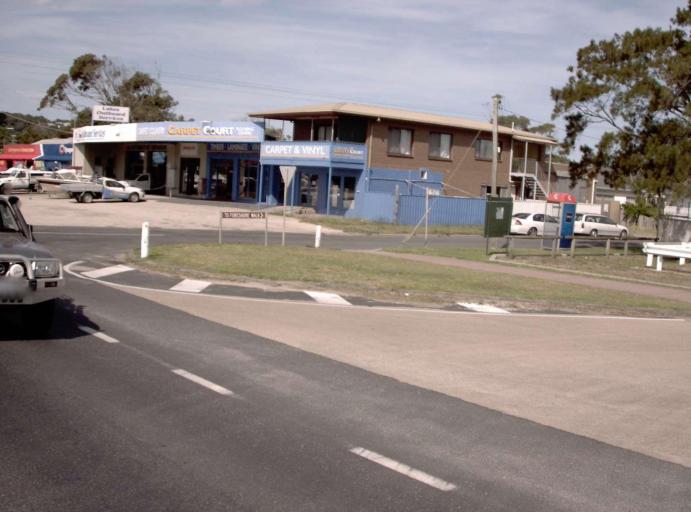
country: AU
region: Victoria
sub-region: East Gippsland
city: Lakes Entrance
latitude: -37.8745
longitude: 148.0078
